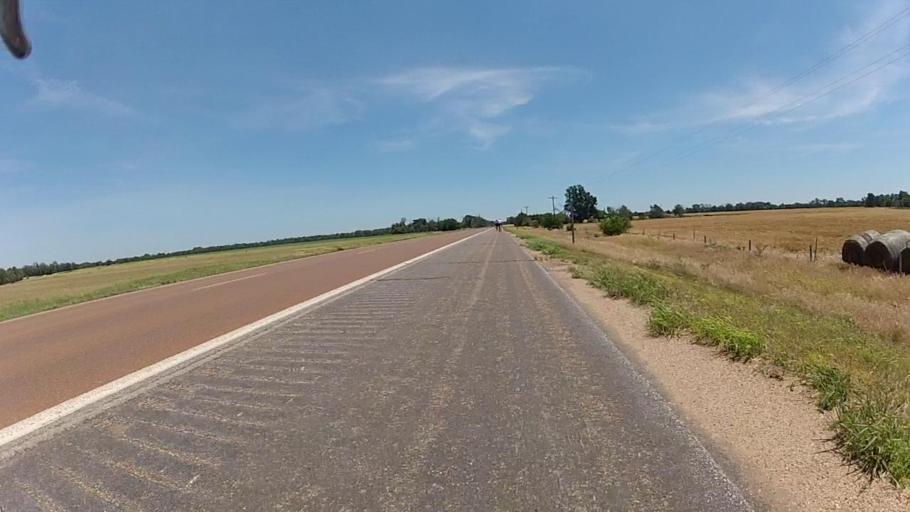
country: US
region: Kansas
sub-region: Barber County
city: Medicine Lodge
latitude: 37.2535
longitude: -98.3432
